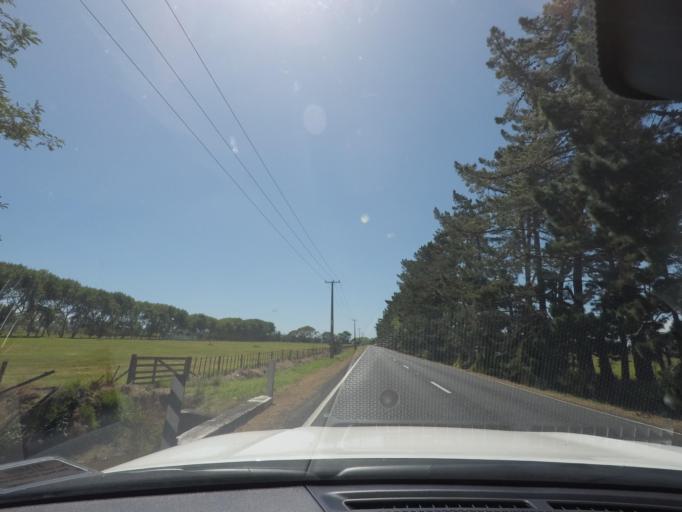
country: NZ
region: Auckland
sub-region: Auckland
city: Parakai
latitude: -36.6541
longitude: 174.4255
